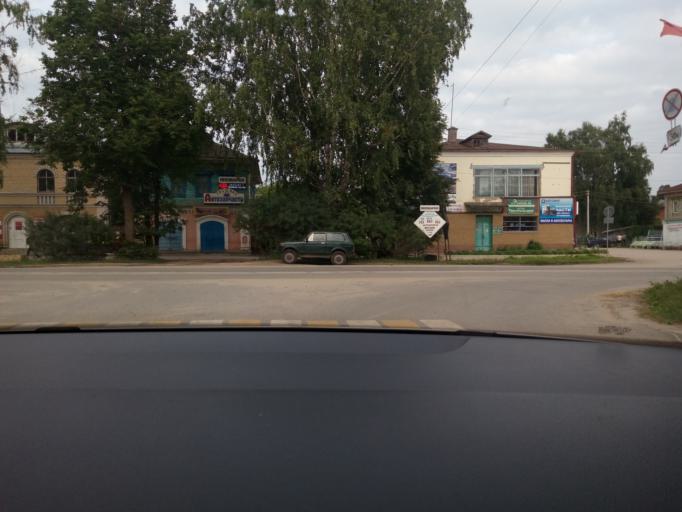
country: RU
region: Nizjnij Novgorod
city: Voskresenskoye
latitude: 56.8383
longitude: 45.4348
